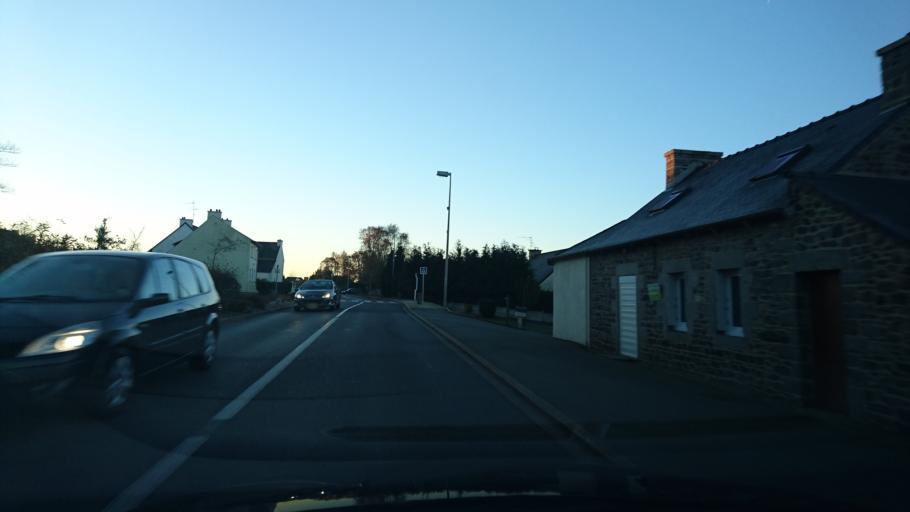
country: FR
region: Brittany
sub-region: Departement des Cotes-d'Armor
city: Pledran
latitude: 48.4514
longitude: -2.7523
